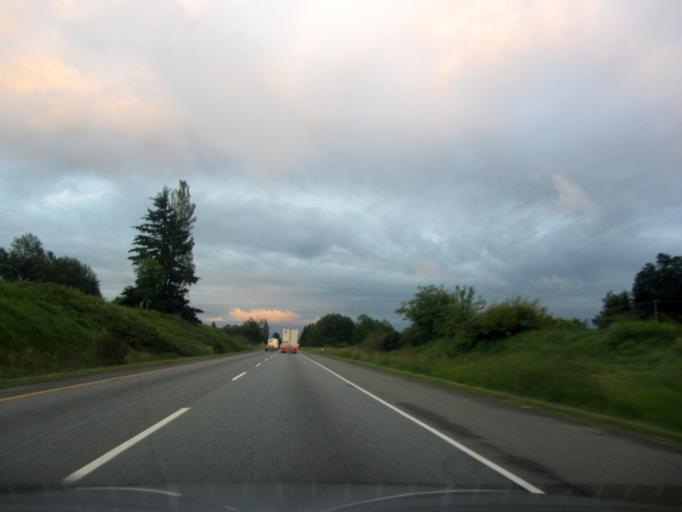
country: CA
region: British Columbia
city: Aldergrove
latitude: 49.0908
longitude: -122.4660
